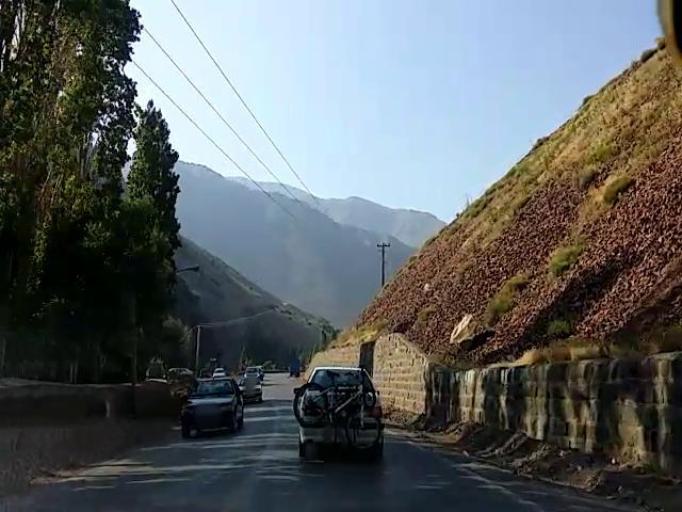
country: IR
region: Tehran
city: Tajrish
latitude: 36.0603
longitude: 51.3099
